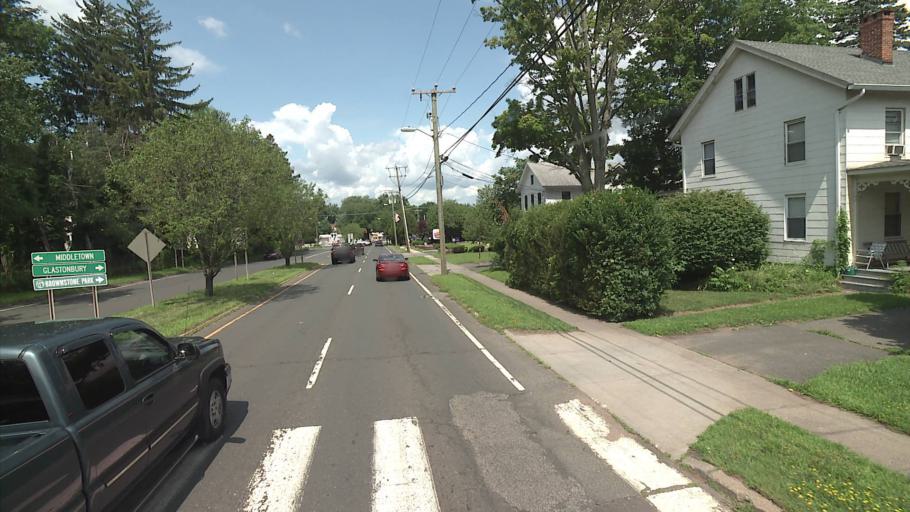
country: US
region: Connecticut
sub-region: Middlesex County
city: Portland
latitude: 41.5724
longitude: -72.6386
